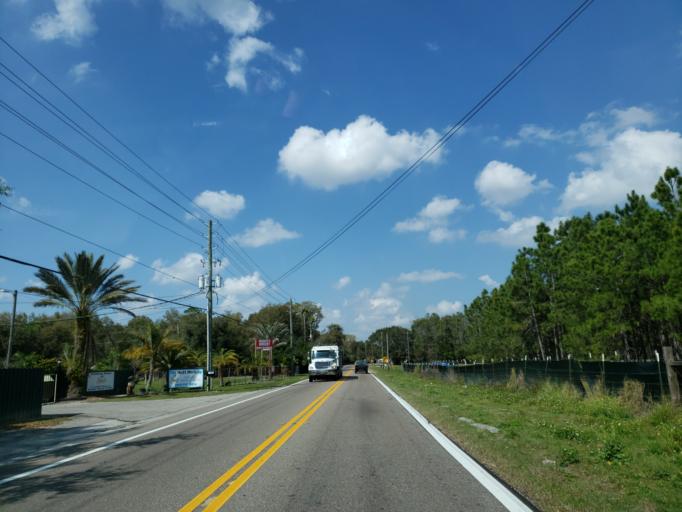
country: US
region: Florida
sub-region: Hillsborough County
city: Keystone
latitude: 28.1457
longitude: -82.5782
